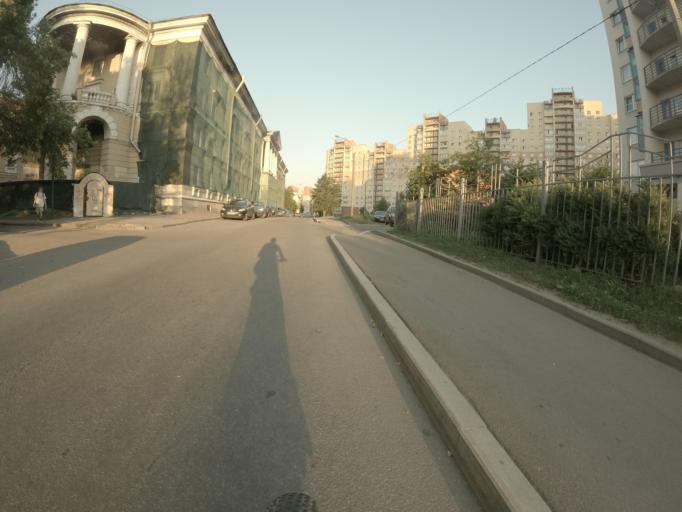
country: RU
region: St.-Petersburg
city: Dachnoye
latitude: 59.8537
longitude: 30.2438
